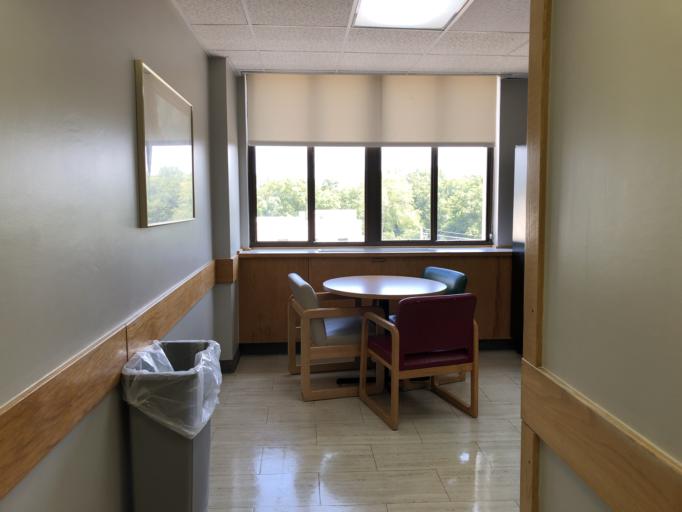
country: US
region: Georgia
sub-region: Clarke County
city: Athens
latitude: 33.9615
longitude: -83.3983
